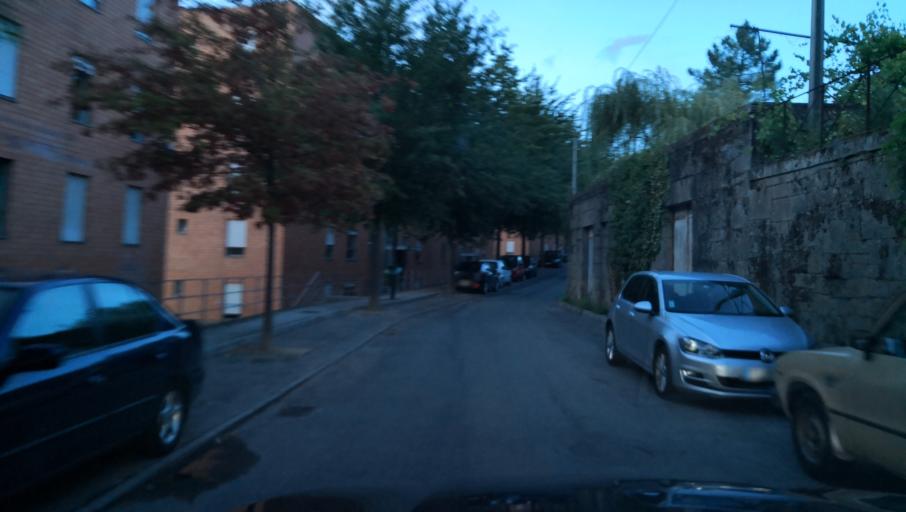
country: PT
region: Vila Real
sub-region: Vila Real
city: Vila Real
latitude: 41.2928
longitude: -7.7586
